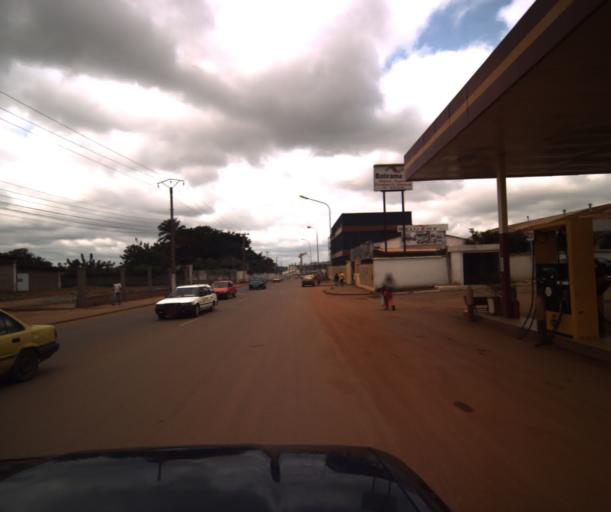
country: CM
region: Centre
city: Yaounde
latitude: 3.8443
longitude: 11.5167
